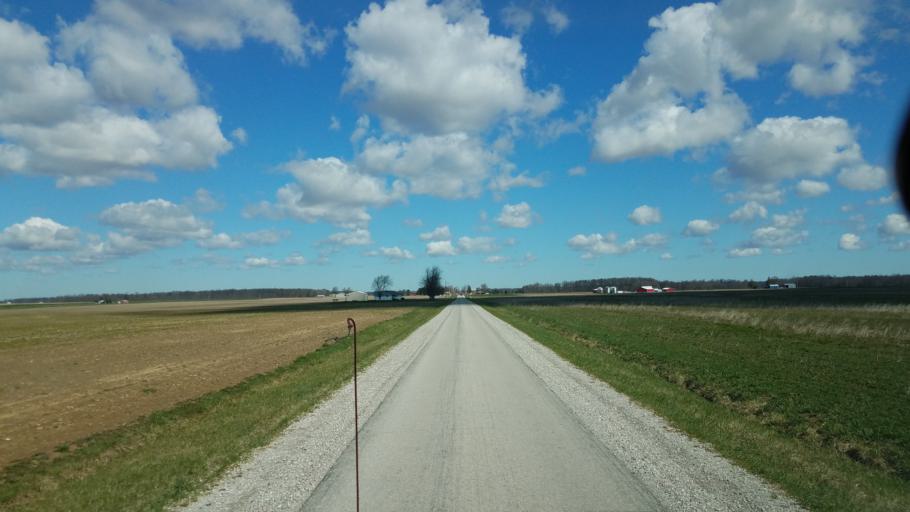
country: US
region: Ohio
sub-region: Sandusky County
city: Mount Carmel
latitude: 41.0998
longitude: -82.9383
